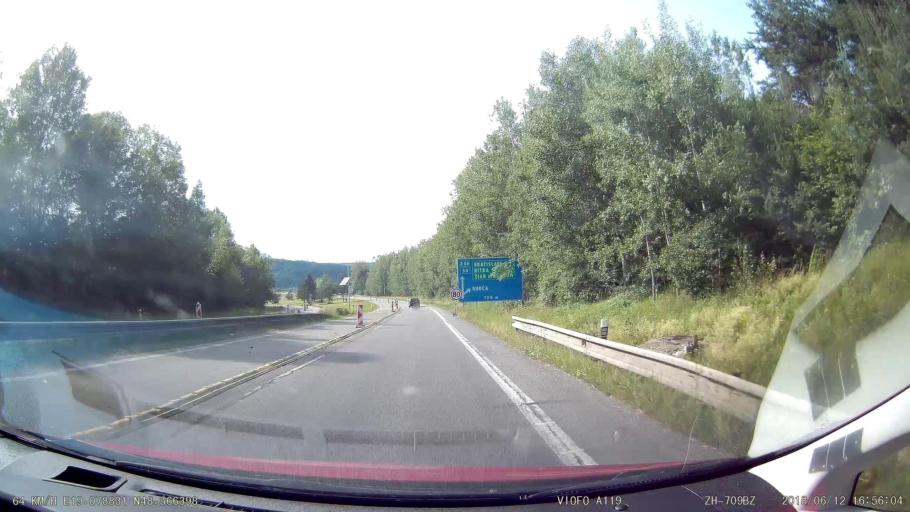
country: SK
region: Banskobystricky
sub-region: Okres Banska Bystrica
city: Zvolen
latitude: 48.5666
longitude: 19.0786
